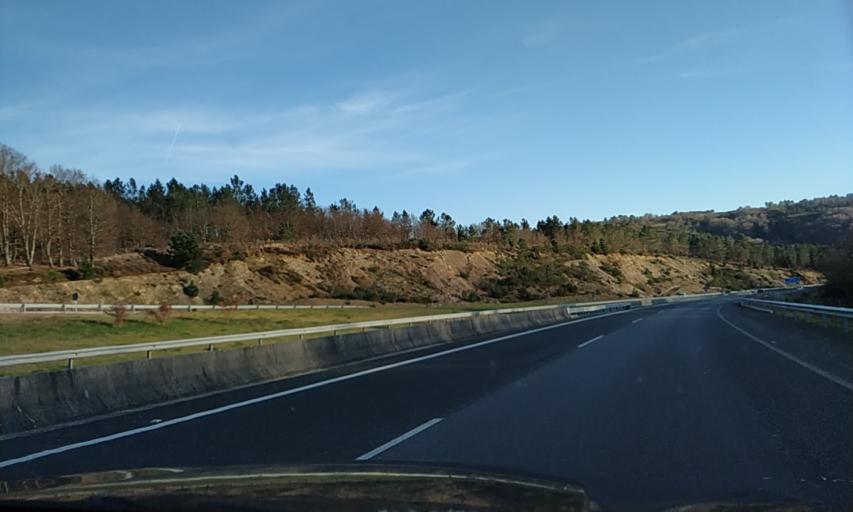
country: ES
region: Galicia
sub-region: Provincia de Pontevedra
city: Lalin
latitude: 42.6198
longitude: -8.0986
